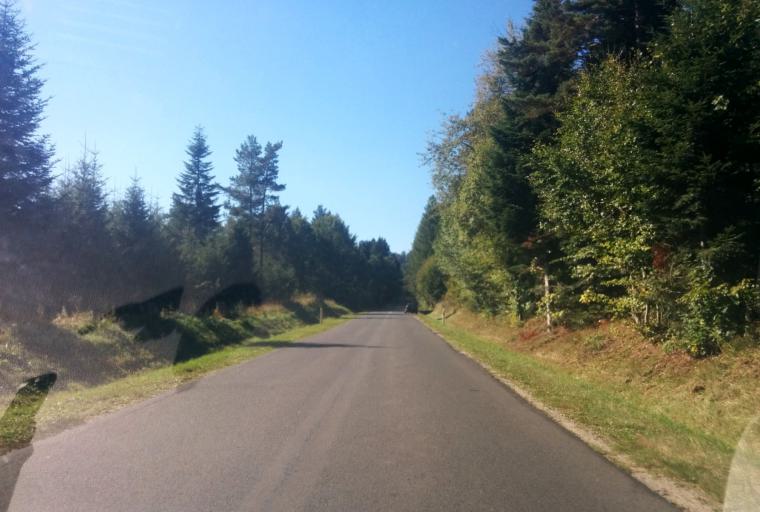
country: PL
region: Subcarpathian Voivodeship
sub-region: Powiat bieszczadzki
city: Czarna
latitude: 49.3135
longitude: 22.6456
